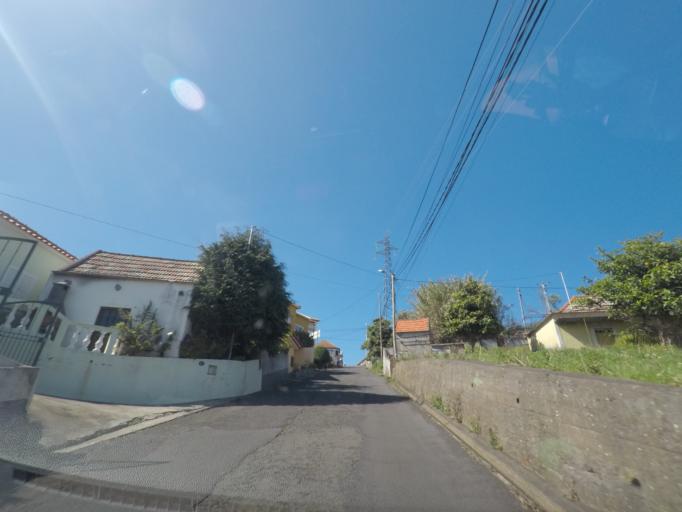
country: PT
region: Madeira
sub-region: Calheta
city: Arco da Calheta
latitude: 32.7082
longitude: -17.1166
